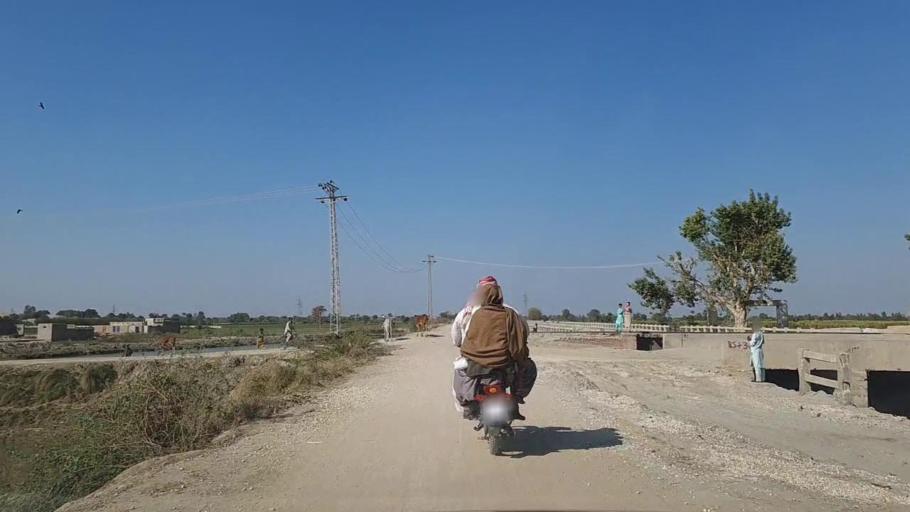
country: PK
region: Sindh
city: Nawabshah
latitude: 26.2602
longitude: 68.4167
